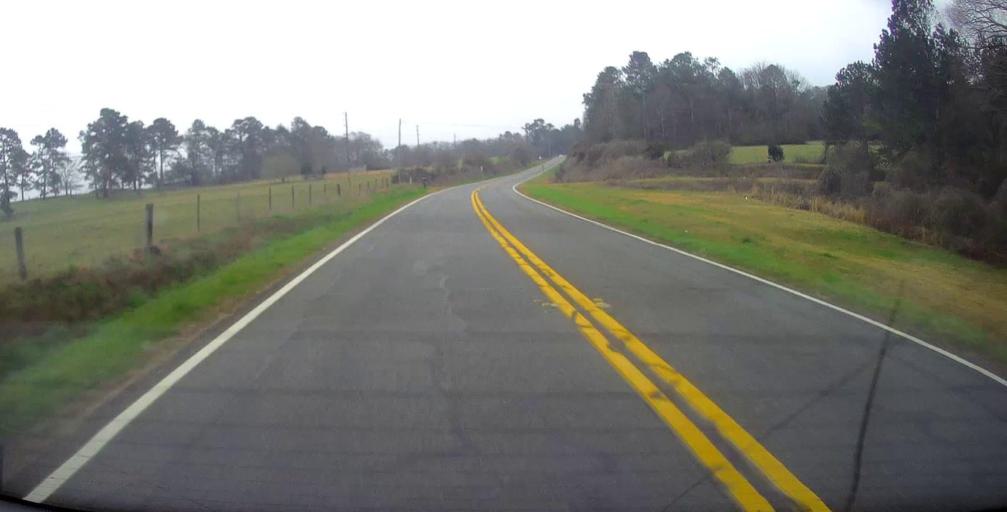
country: US
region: Georgia
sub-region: Monroe County
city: Forsyth
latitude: 33.1008
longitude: -83.9439
